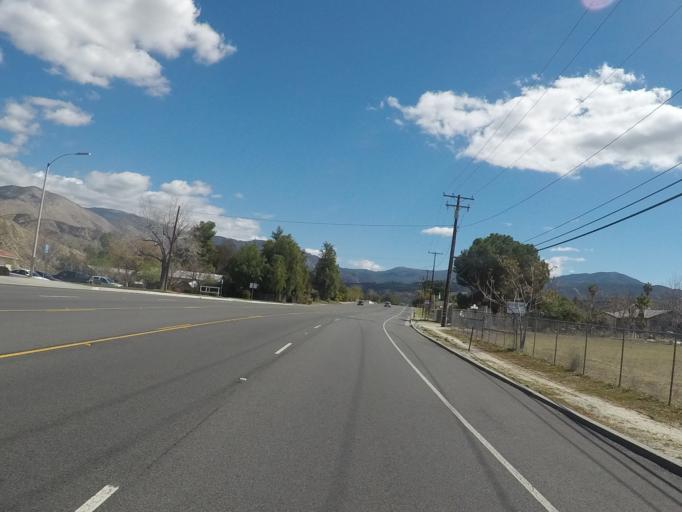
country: US
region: California
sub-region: Riverside County
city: Valle Vista
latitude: 33.7476
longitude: -116.8709
